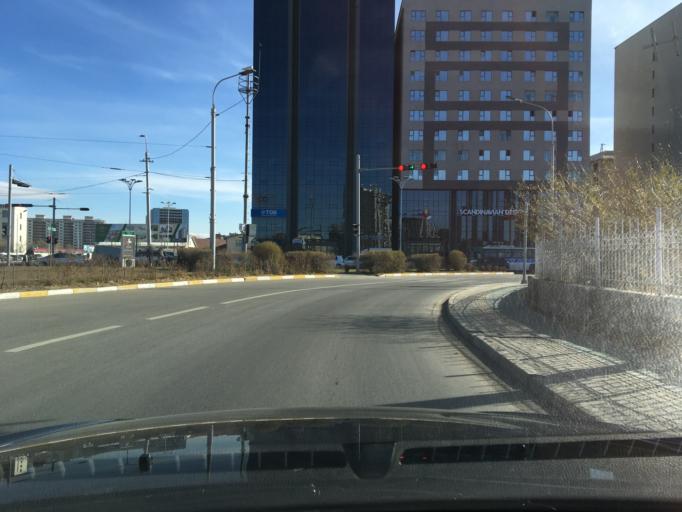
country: MN
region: Ulaanbaatar
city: Ulaanbaatar
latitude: 47.8991
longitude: 106.9083
